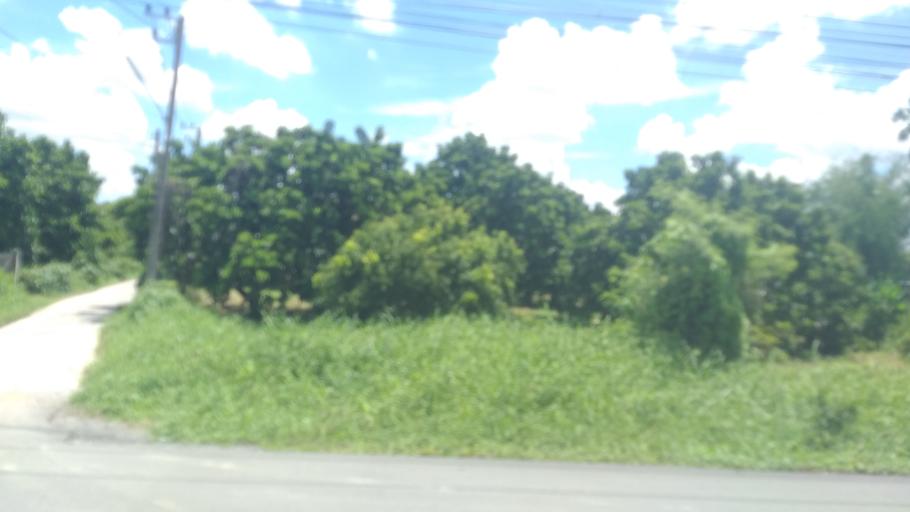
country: TH
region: Nakhon Nayok
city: Ban Na
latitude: 14.2880
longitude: 101.0673
